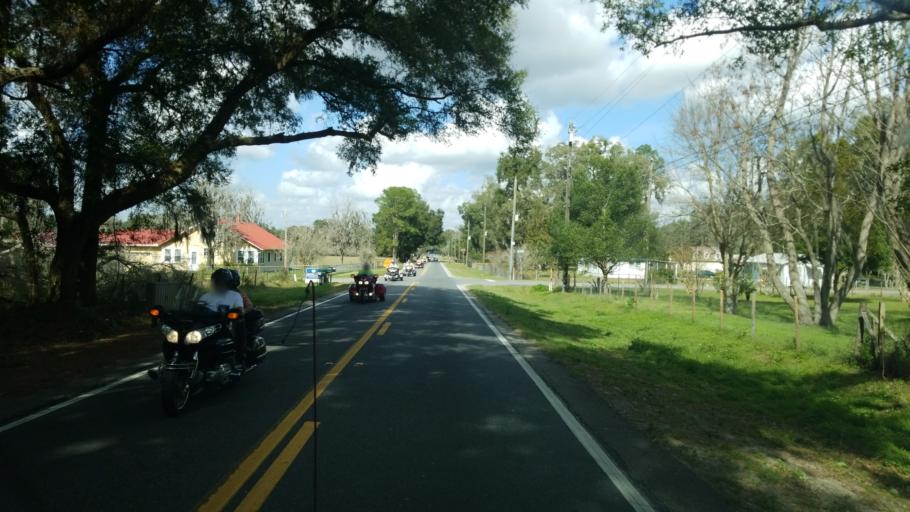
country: US
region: Florida
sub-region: Marion County
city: Belleview
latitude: 29.0032
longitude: -82.1199
